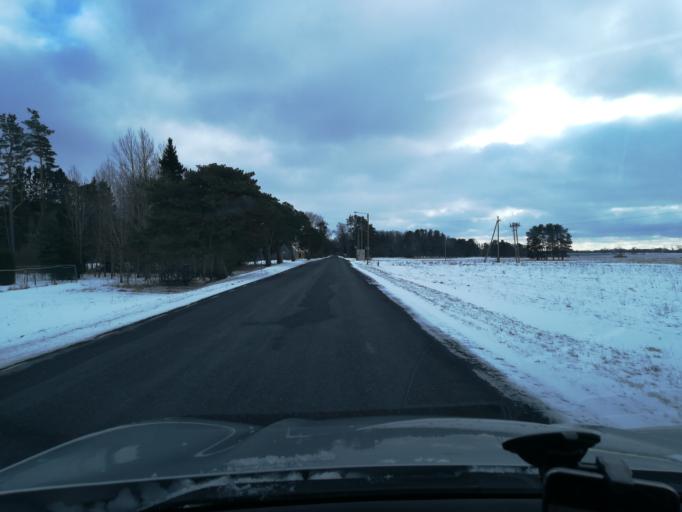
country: EE
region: Harju
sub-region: Keila linn
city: Keila
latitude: 59.3976
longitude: 24.4127
